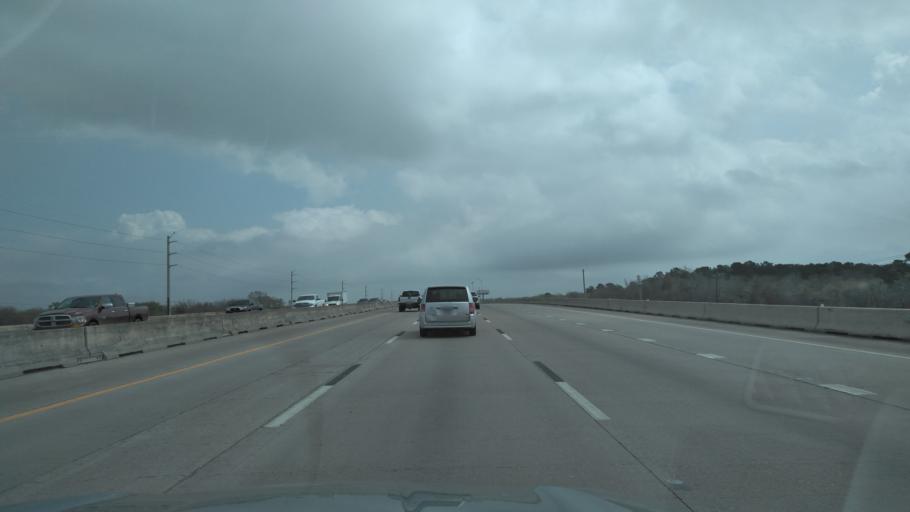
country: US
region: Texas
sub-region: Harris County
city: Highlands
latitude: 29.7999
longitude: -95.0181
